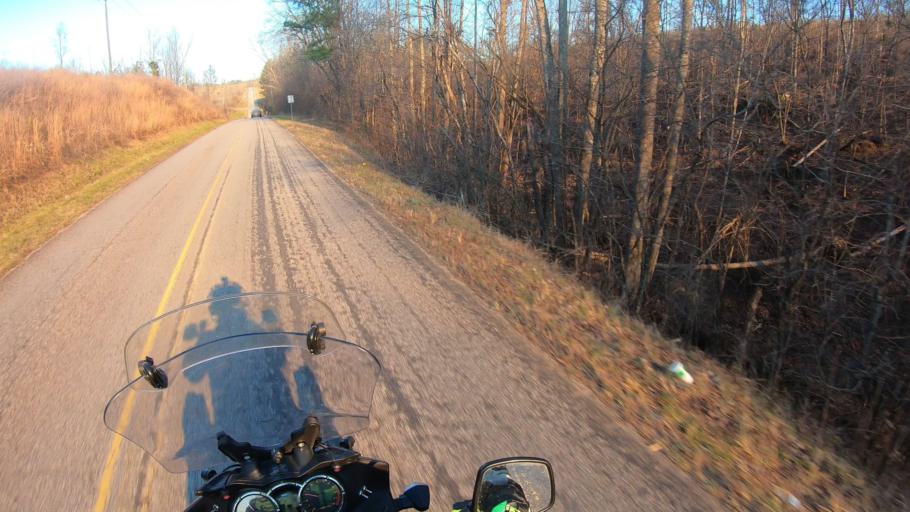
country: US
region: Georgia
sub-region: Haralson County
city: Tallapoosa
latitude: 33.7776
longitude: -85.4530
